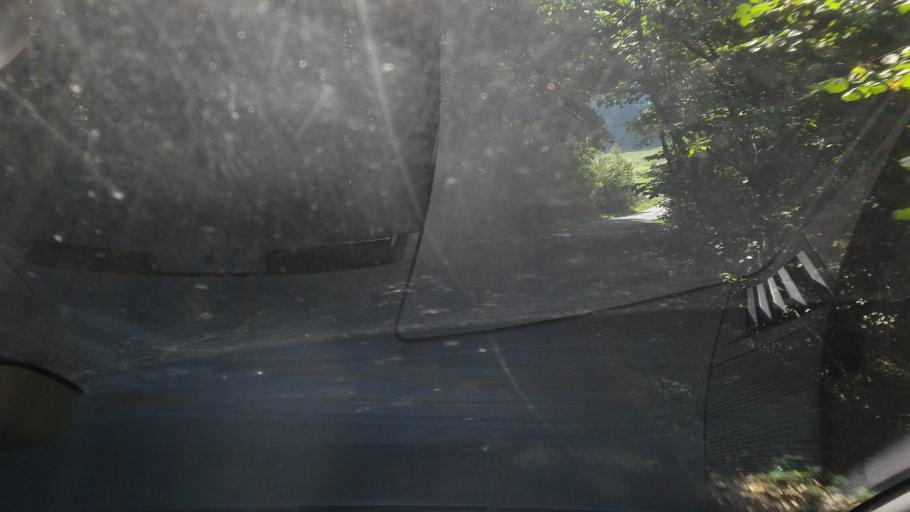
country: BE
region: Wallonia
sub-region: Province du Luxembourg
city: Arlon
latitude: 49.7124
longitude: 5.8386
